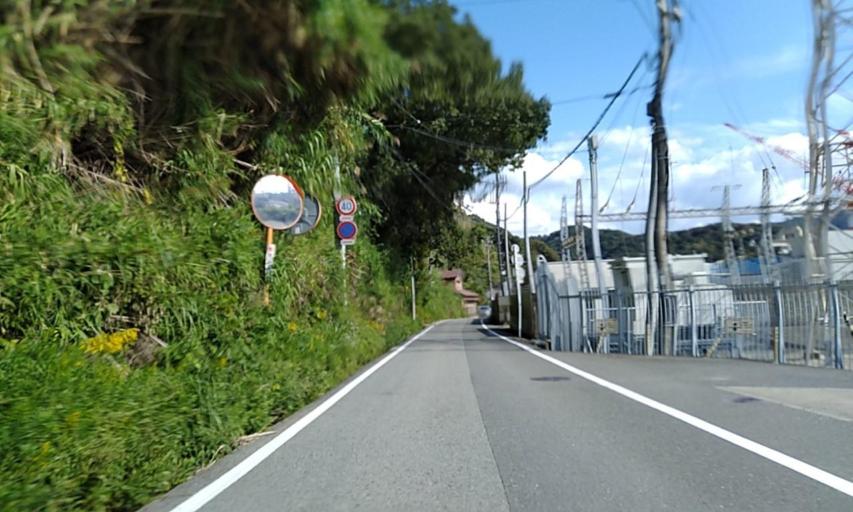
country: JP
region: Wakayama
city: Gobo
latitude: 33.9645
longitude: 135.1083
